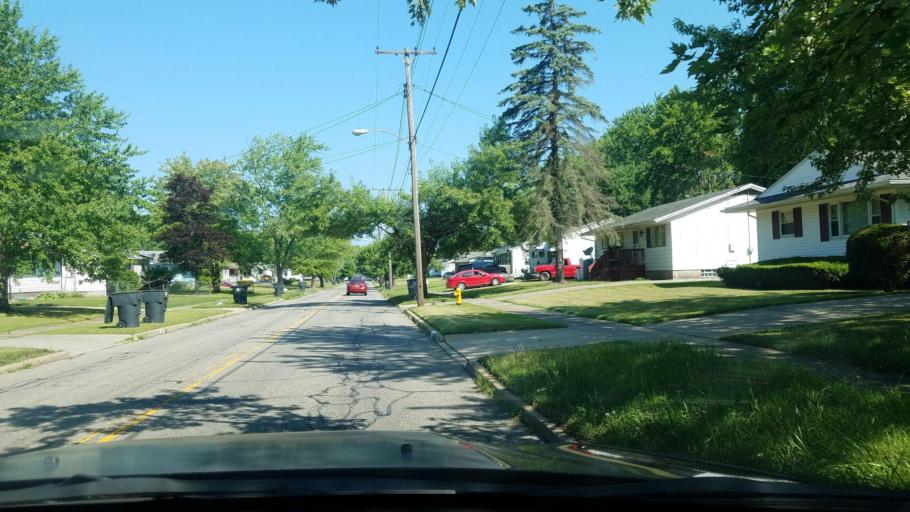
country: US
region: Ohio
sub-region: Trumbull County
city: Leavittsburg
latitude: 41.2479
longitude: -80.8559
